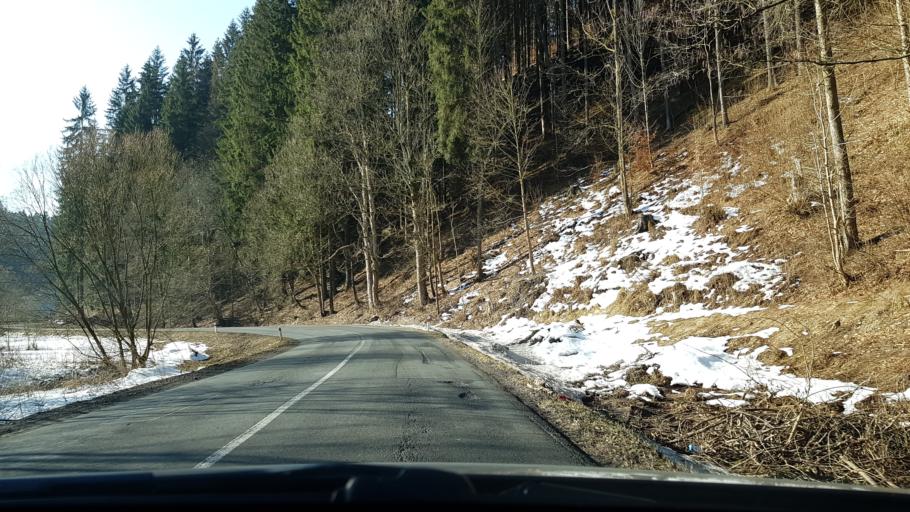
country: CZ
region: Olomoucky
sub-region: Okres Sumperk
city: Hanusovice
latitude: 50.0852
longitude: 16.9699
